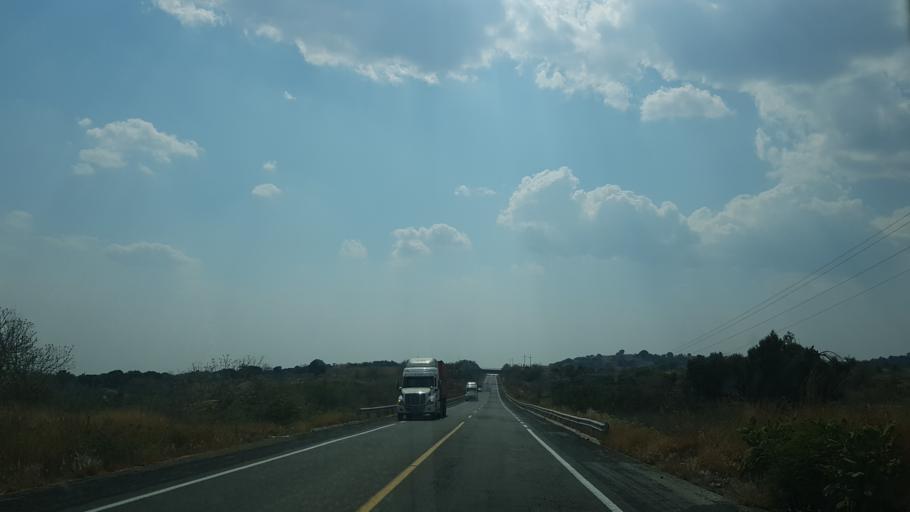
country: MX
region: Puebla
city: San Juan Amecac
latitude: 18.8167
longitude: -98.6593
